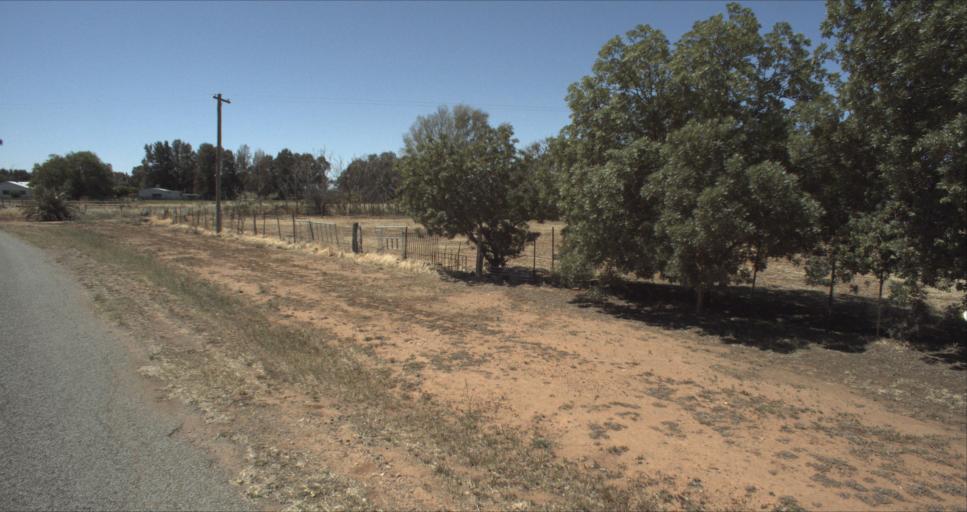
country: AU
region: New South Wales
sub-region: Leeton
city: Leeton
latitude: -34.5268
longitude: 146.3334
